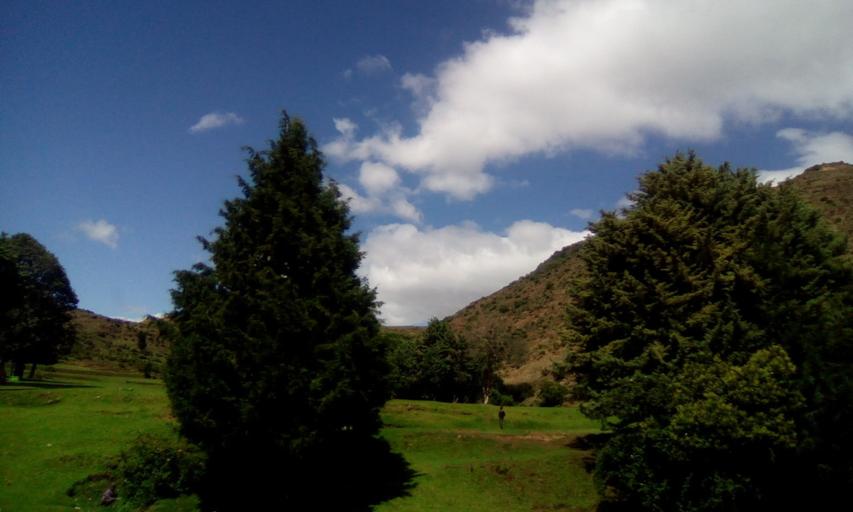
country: LS
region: Maseru
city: Nako
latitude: -29.6622
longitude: 27.7870
